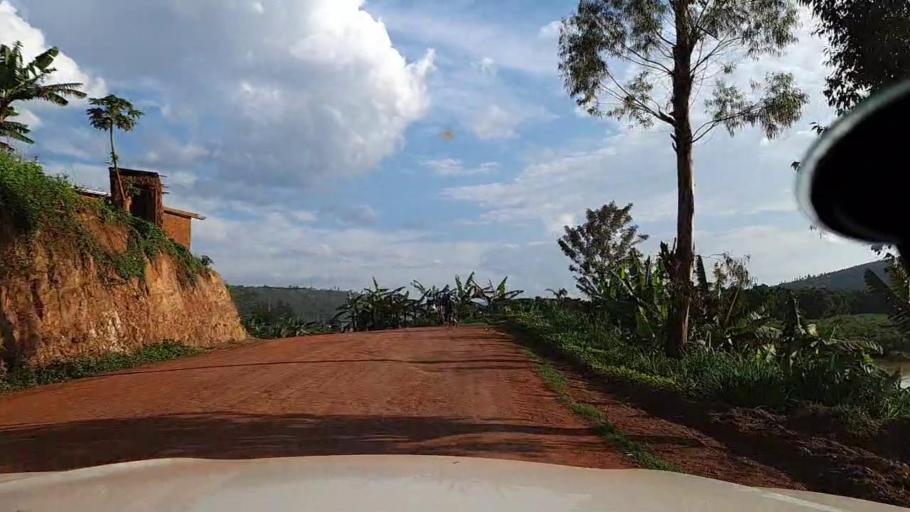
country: RW
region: Kigali
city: Kigali
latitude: -1.9372
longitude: 29.9982
